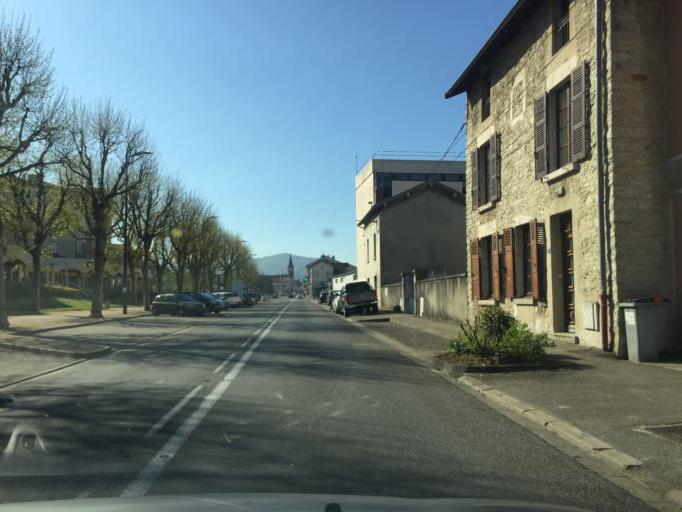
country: FR
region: Rhone-Alpes
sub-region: Departement de l'Ain
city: Amberieu-en-Bugey
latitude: 45.9632
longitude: 5.3564
